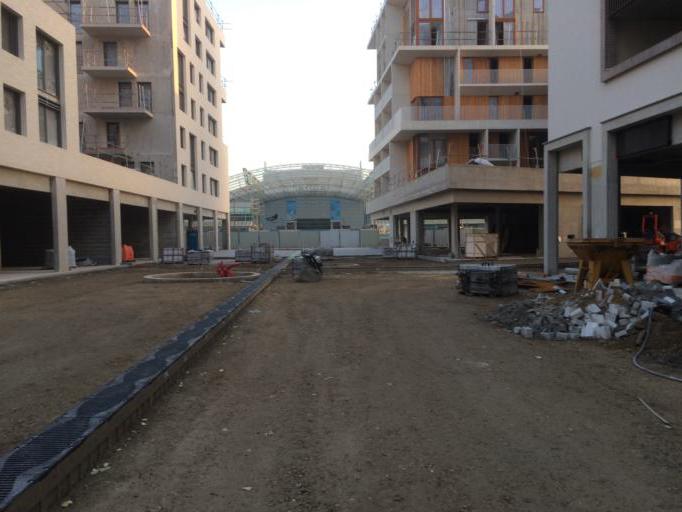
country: FR
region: Ile-de-France
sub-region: Departement de l'Essonne
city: Massy
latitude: 48.7332
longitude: 2.2888
